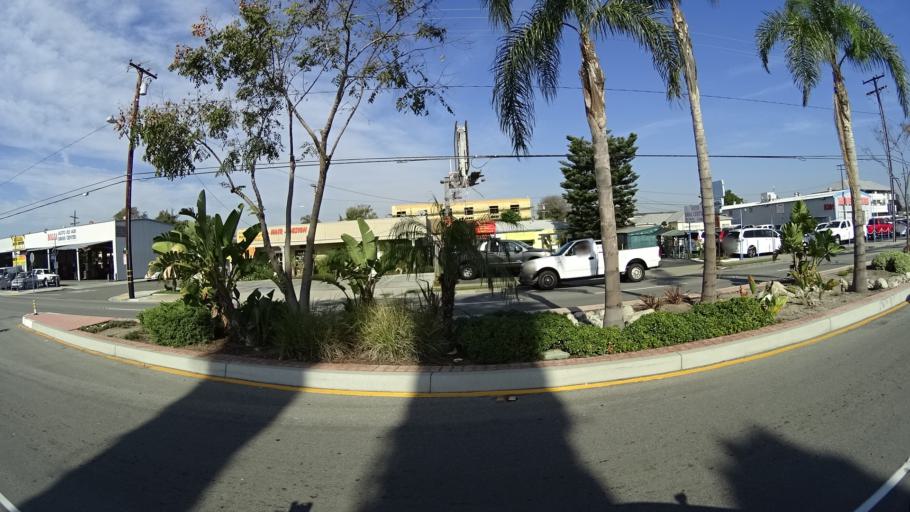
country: US
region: California
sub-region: Orange County
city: Midway City
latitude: 33.7445
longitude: -117.9827
